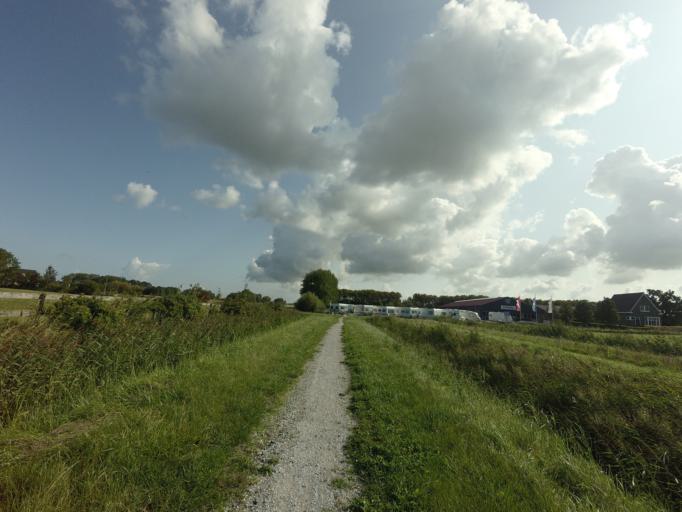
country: NL
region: Friesland
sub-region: Gemeente Franekeradeel
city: Tzummarum
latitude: 53.2408
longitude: 5.5415
